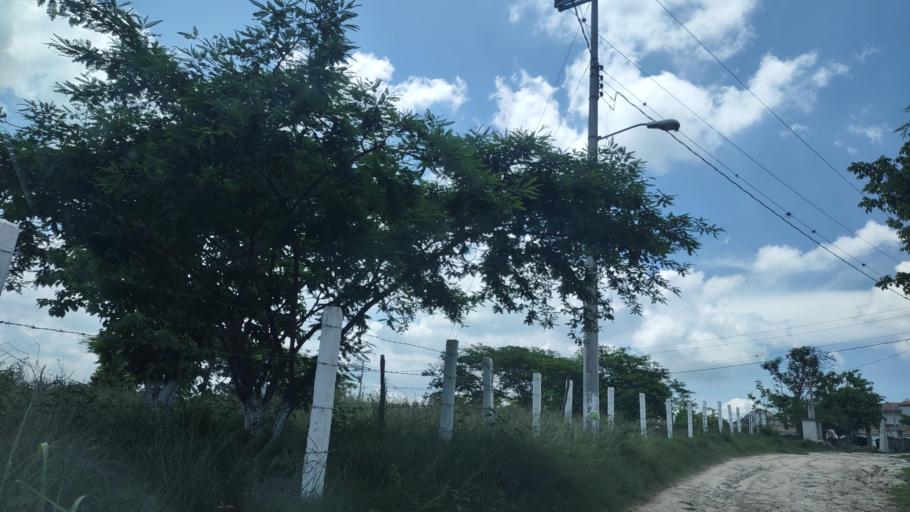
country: MX
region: Veracruz
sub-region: Emiliano Zapata
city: Dos Rios
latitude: 19.5013
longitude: -96.8126
